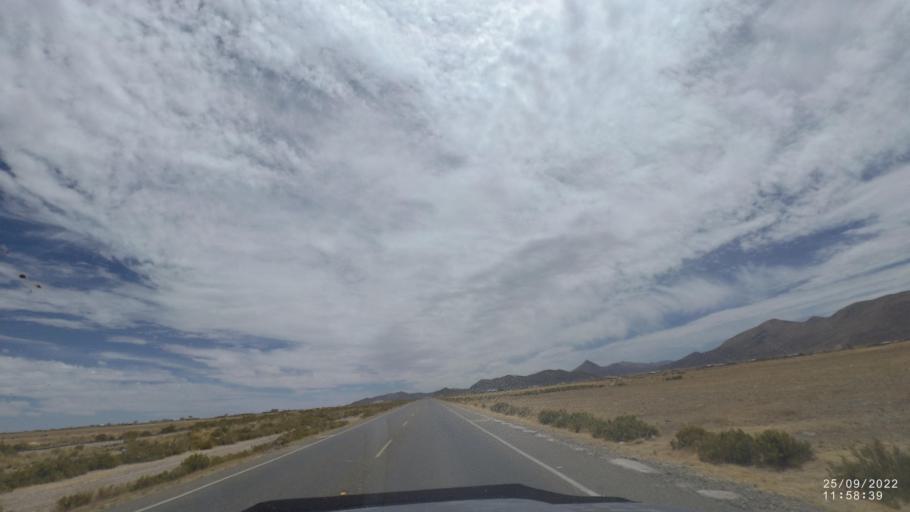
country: BO
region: Oruro
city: Challapata
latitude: -18.8009
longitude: -66.8395
